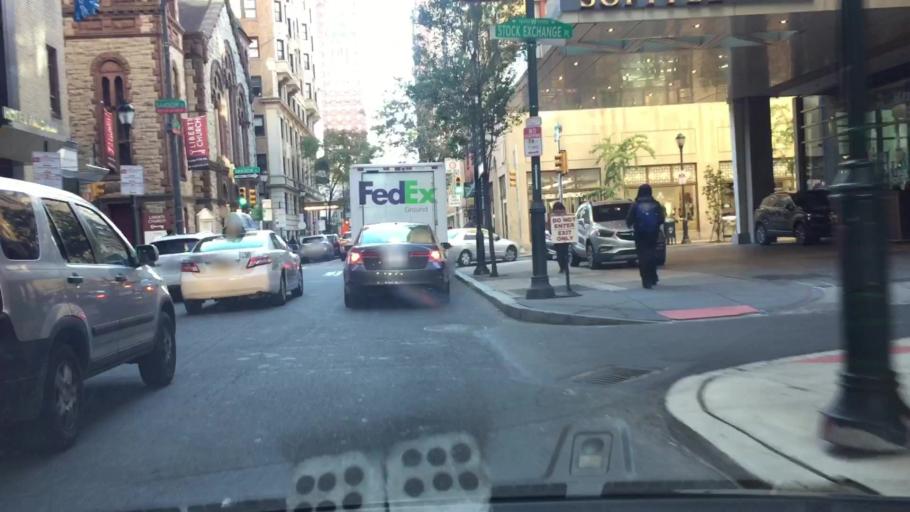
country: US
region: Pennsylvania
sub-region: Philadelphia County
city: Philadelphia
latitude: 39.9511
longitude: -75.1689
